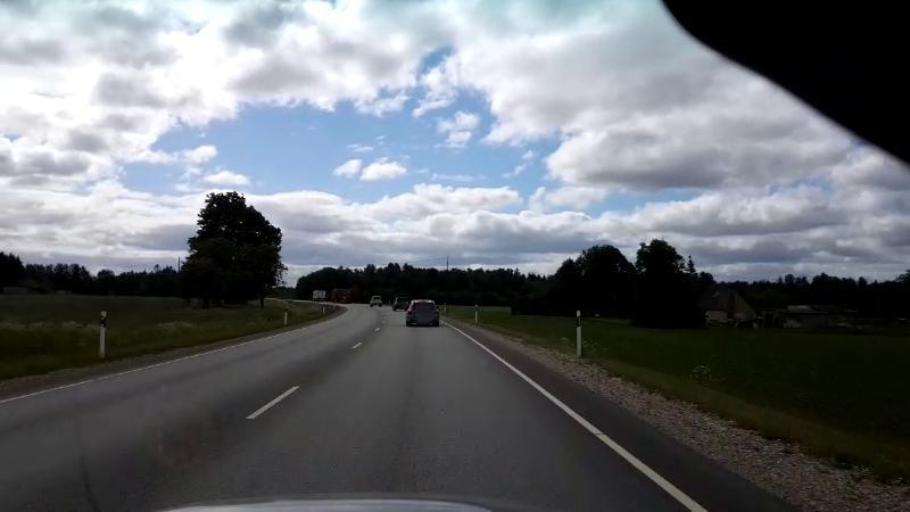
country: EE
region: Paernumaa
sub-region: Halinga vald
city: Parnu-Jaagupi
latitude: 58.5626
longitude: 24.5181
